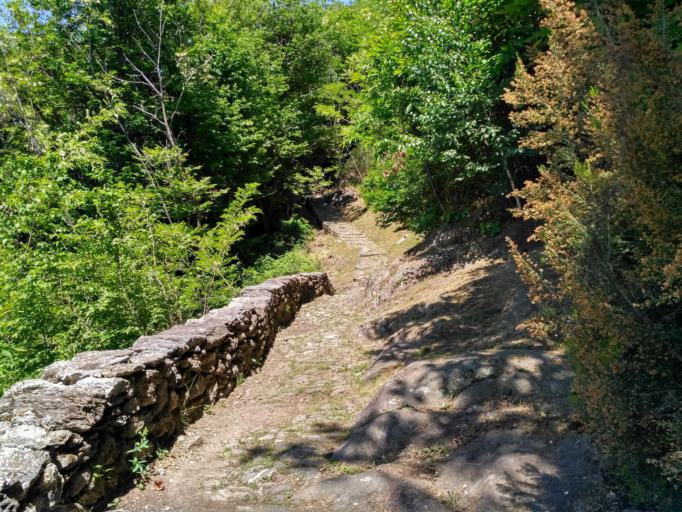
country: IT
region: Lombardy
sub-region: Provincia di Lecco
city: Dorio
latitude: 46.1062
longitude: 9.3238
